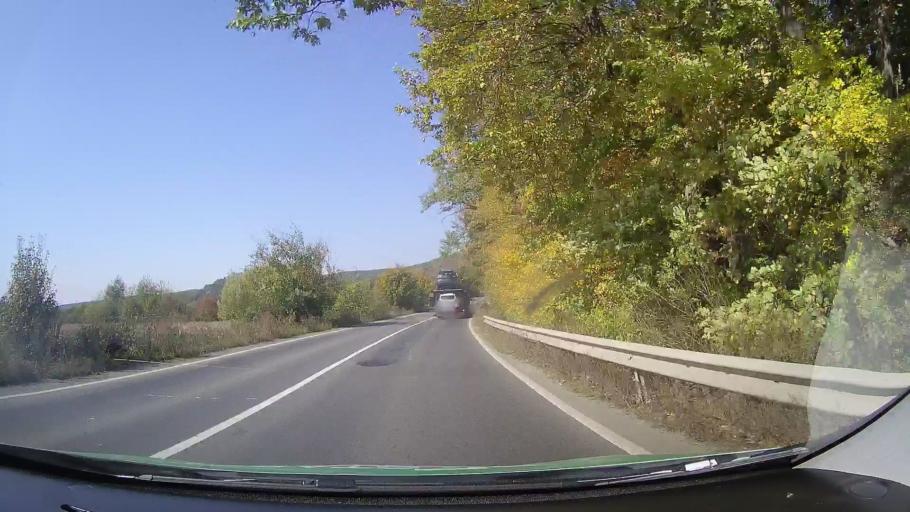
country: RO
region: Arad
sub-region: Comuna Conop
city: Conop
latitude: 46.1100
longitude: 21.8501
